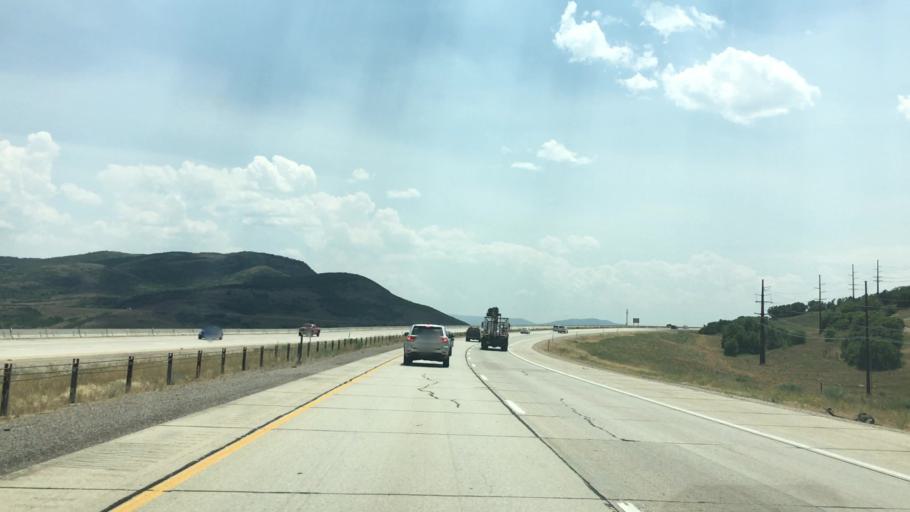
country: US
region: Utah
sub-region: Summit County
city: Park City
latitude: 40.6087
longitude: -111.4295
